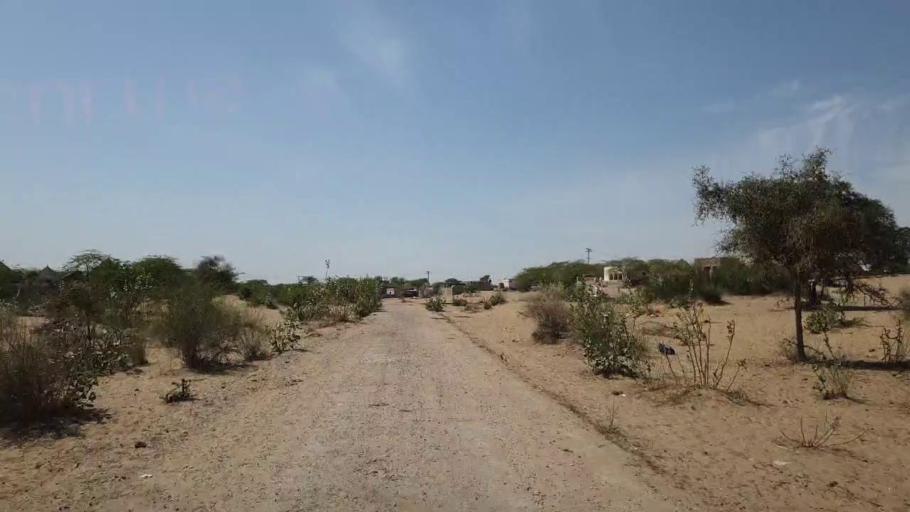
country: PK
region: Sindh
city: Umarkot
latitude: 25.1936
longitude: 69.8939
